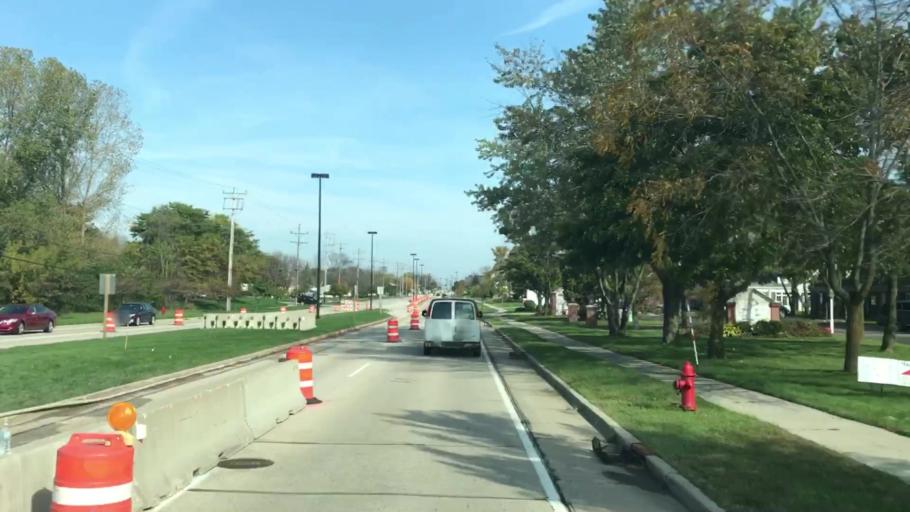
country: US
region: Wisconsin
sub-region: Milwaukee County
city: River Hills
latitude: 43.2022
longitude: -87.9242
